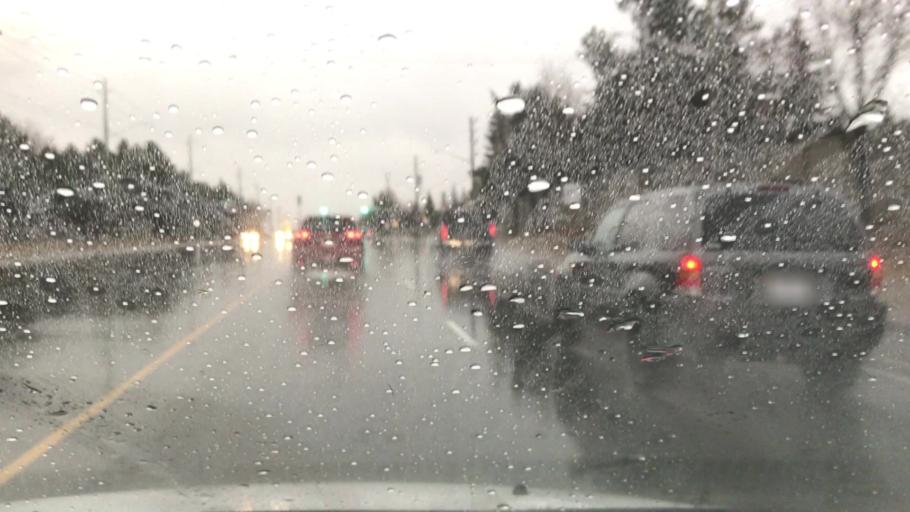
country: CA
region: Ontario
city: Newmarket
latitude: 44.0442
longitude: -79.4268
